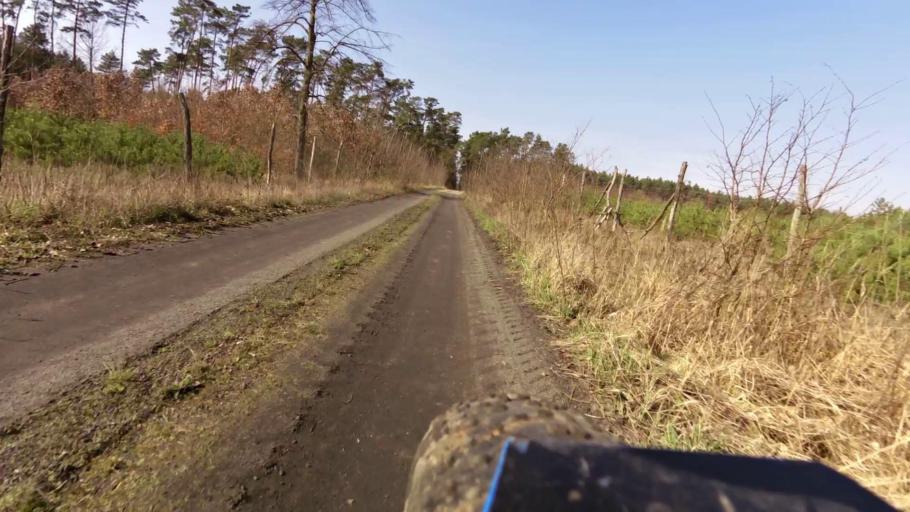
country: PL
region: Lubusz
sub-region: Powiat slubicki
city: Cybinka
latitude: 52.2101
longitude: 14.8636
